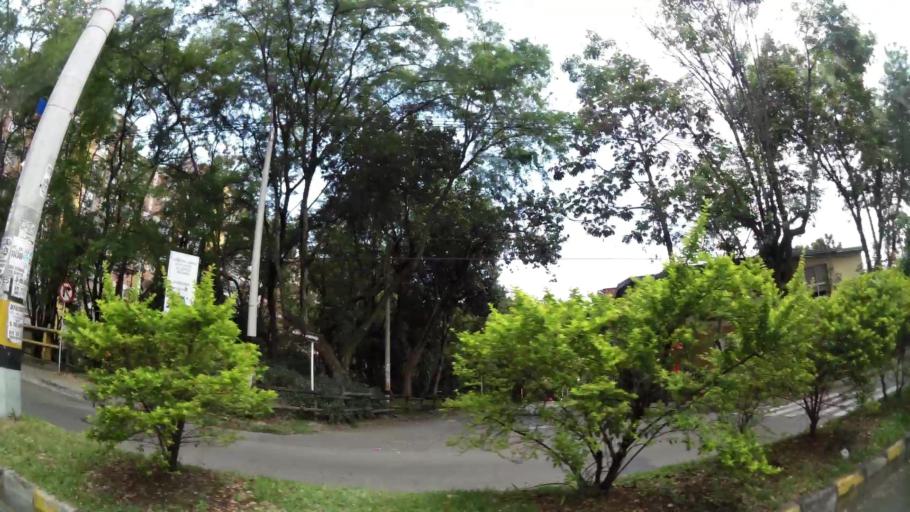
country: CO
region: Antioquia
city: Medellin
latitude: 6.2449
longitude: -75.6135
